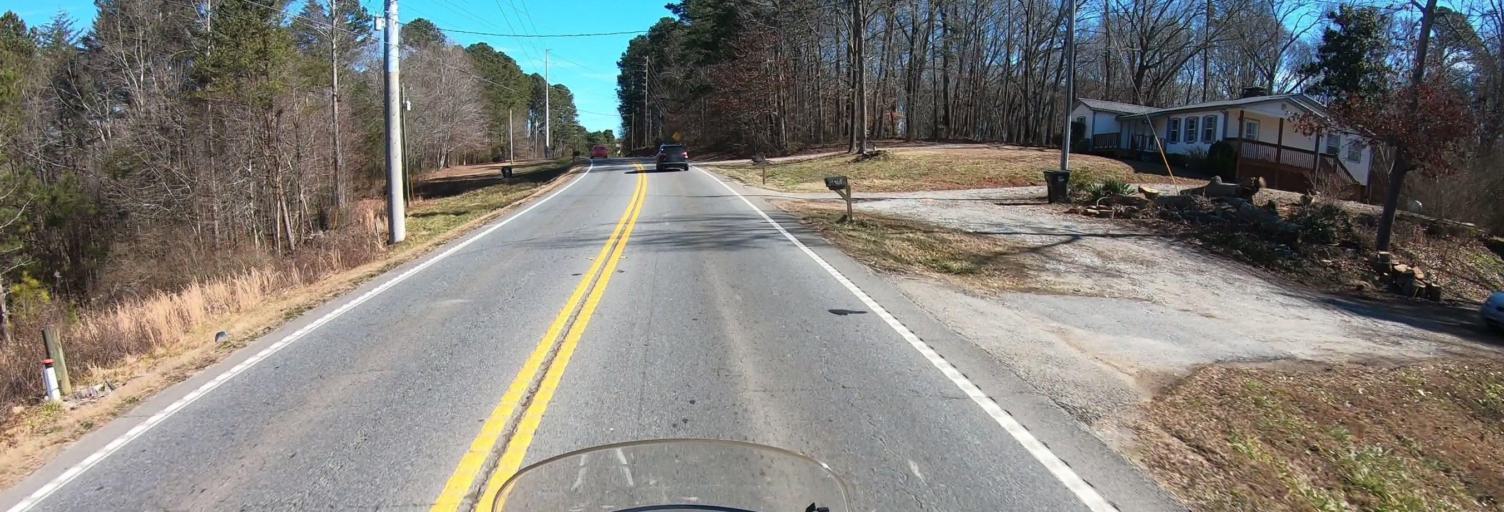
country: US
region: Georgia
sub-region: Forsyth County
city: Cumming
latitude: 34.3003
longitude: -84.1712
